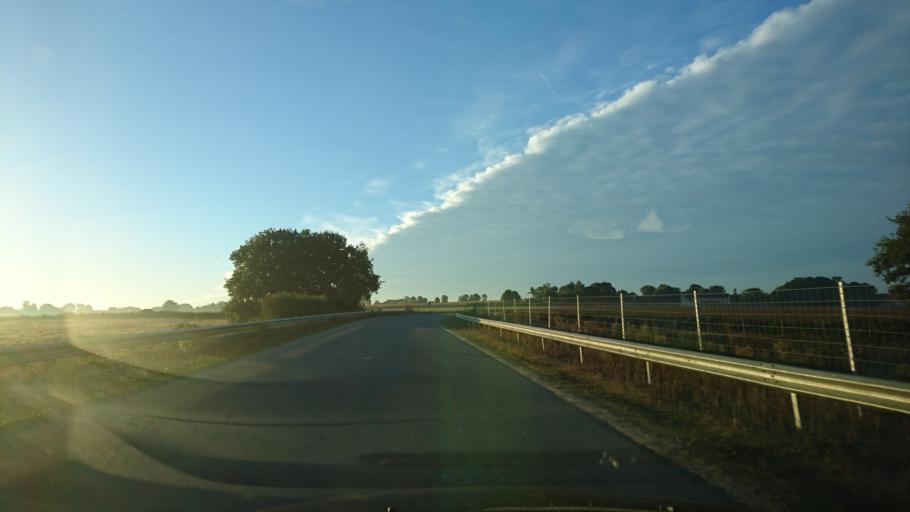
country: FR
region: Brittany
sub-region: Departement d'Ille-et-Vilaine
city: Sainte-Marie
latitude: 47.7082
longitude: -1.9942
